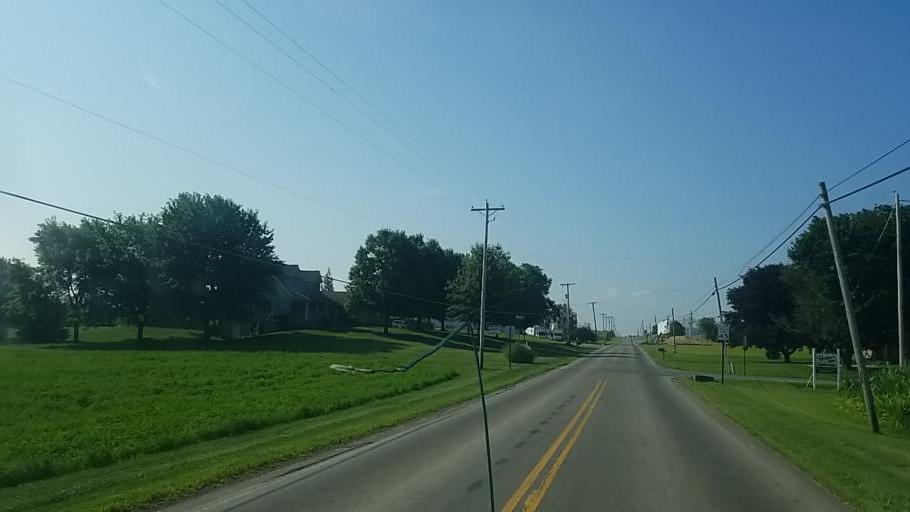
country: US
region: Ohio
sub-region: Wayne County
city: Dalton
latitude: 40.7319
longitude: -81.7451
